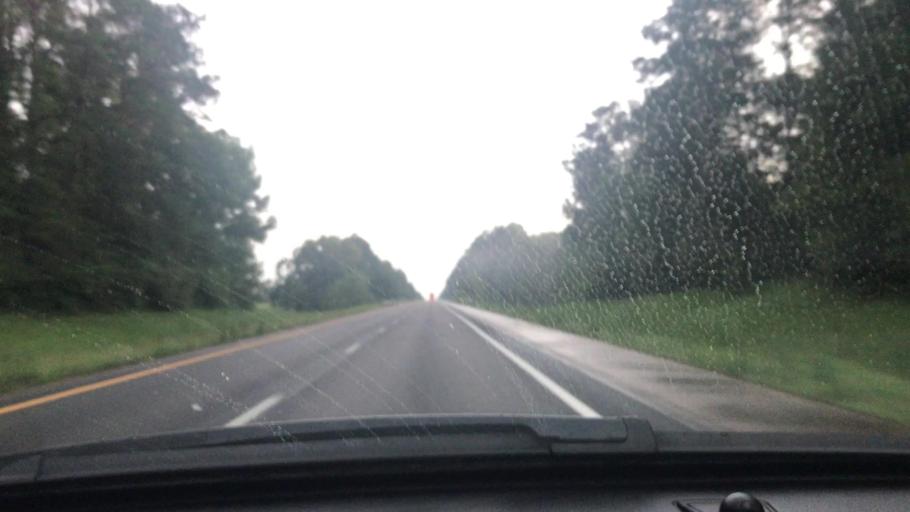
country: US
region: Mississippi
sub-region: Pike County
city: Magnolia
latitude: 31.0946
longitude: -90.4885
